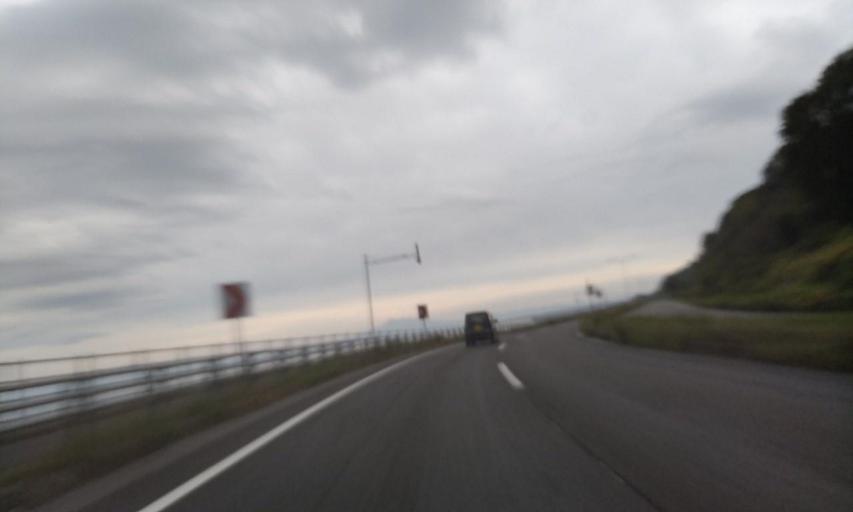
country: JP
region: Hokkaido
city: Abashiri
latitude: 44.0020
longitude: 144.2889
